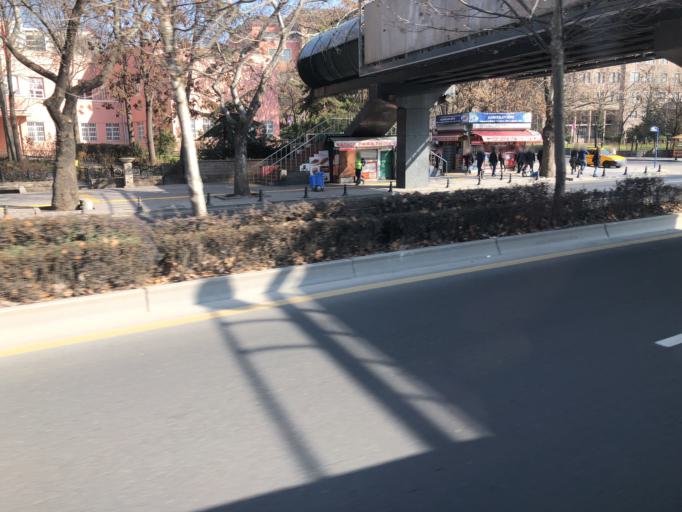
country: TR
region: Ankara
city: Ankara
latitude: 39.9310
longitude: 32.8542
